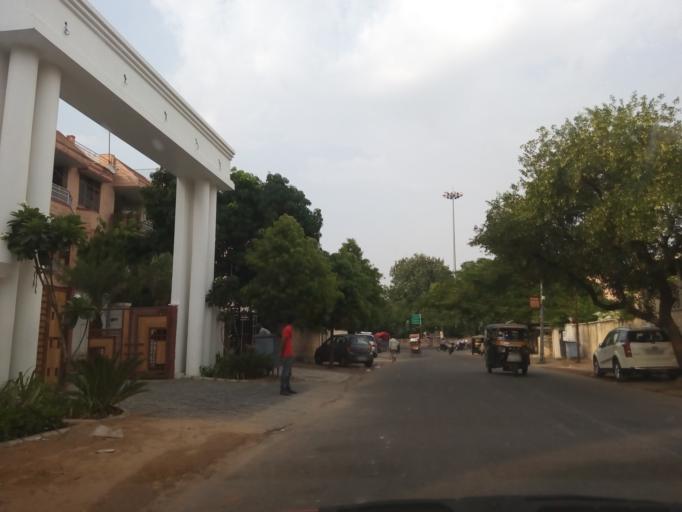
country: IN
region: Rajasthan
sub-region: Jaipur
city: Jaipur
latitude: 26.9281
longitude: 75.7968
